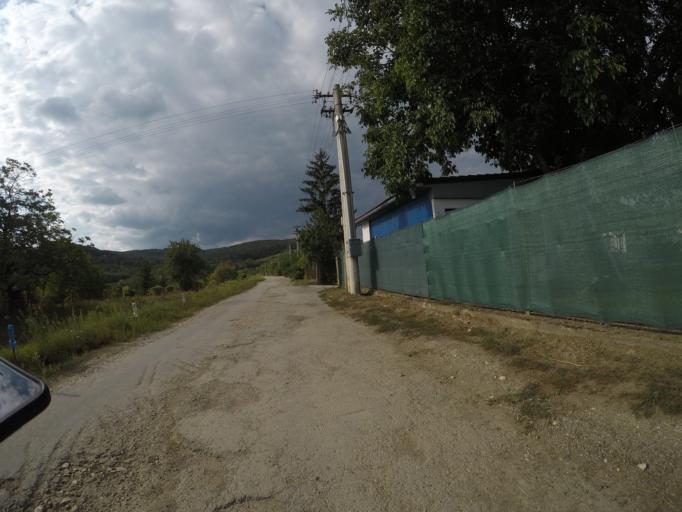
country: SK
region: Trenciansky
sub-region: Okres Trencin
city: Trencin
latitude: 48.9003
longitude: 17.9947
